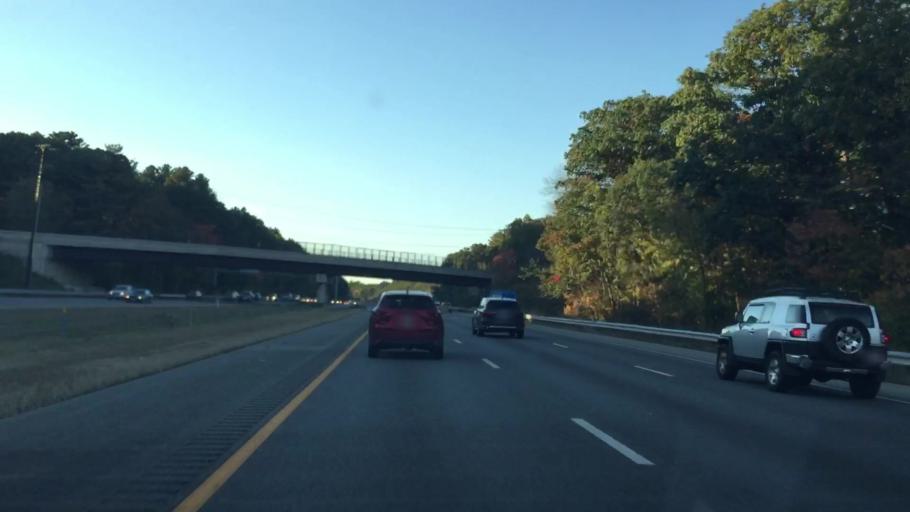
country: US
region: Massachusetts
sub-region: Middlesex County
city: Bedford
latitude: 42.5169
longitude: -71.2579
